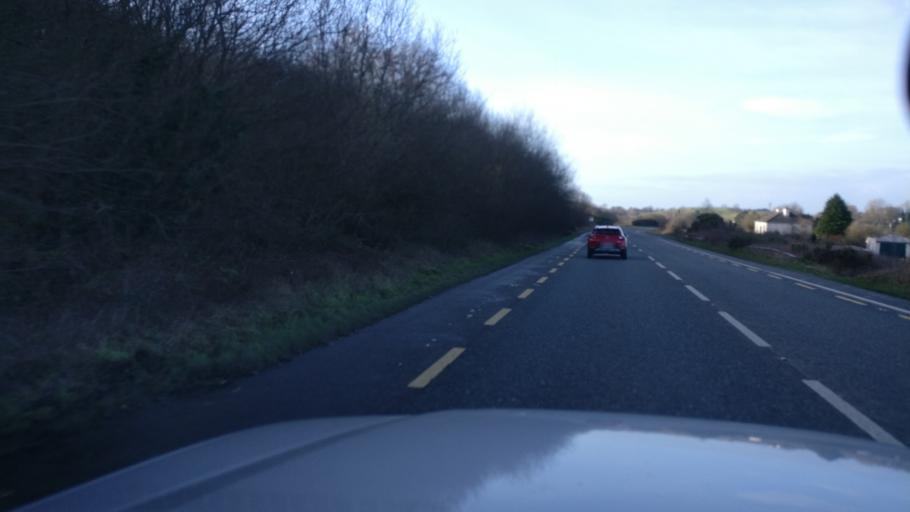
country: IE
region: Leinster
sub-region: Uibh Fhaili
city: Clara
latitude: 53.3275
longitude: -7.5863
